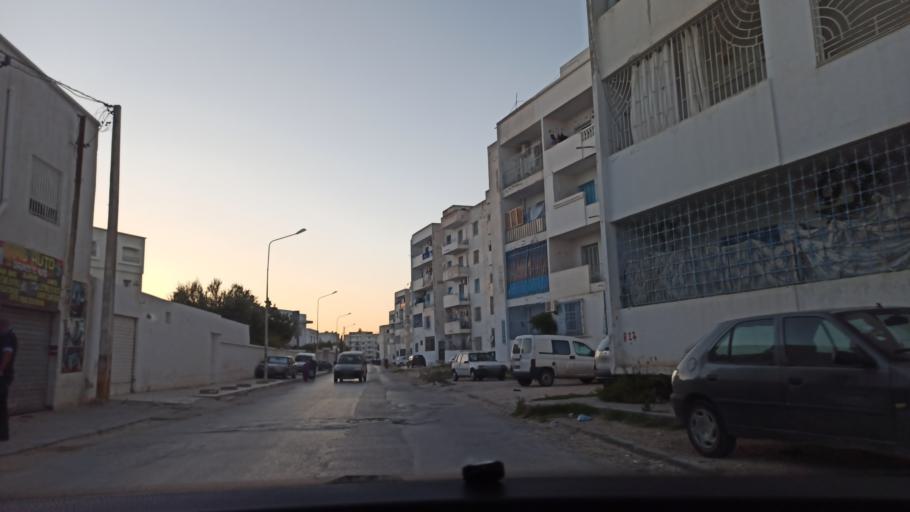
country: TN
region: Ariana
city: Ariana
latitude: 36.8658
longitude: 10.1975
